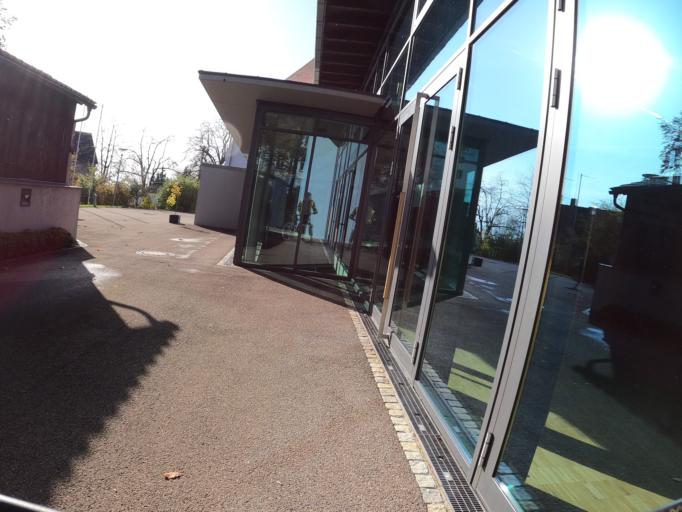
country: DE
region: Bavaria
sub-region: Swabia
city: Nersingen
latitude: 48.4525
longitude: 10.0861
